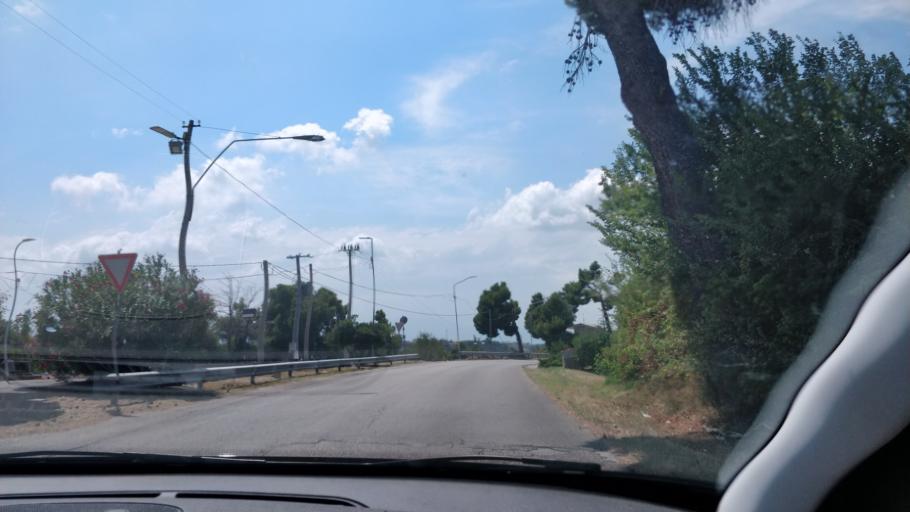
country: IT
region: Abruzzo
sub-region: Provincia di Chieti
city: Torrevecchia
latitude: 42.4091
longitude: 14.2251
